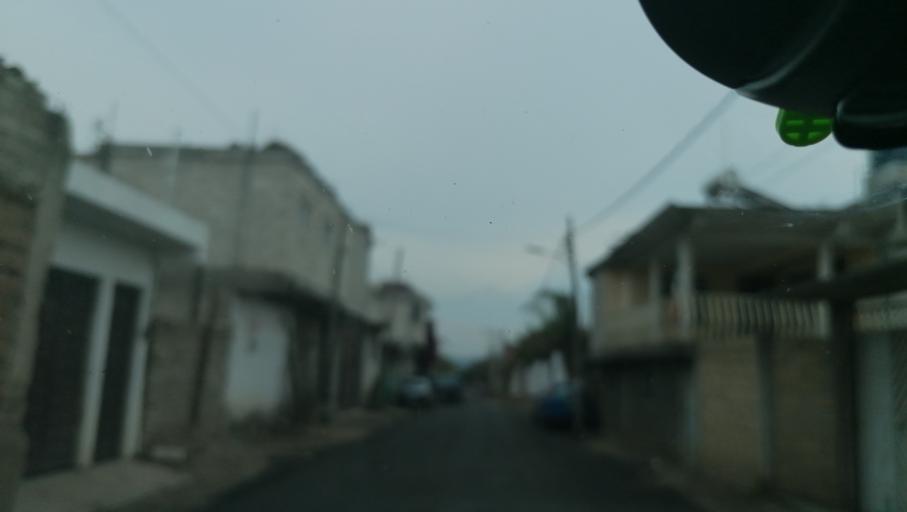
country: MX
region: Puebla
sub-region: Santa Isabel Cholula
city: Santa Isabel Cholula
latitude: 19.0115
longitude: -98.4013
